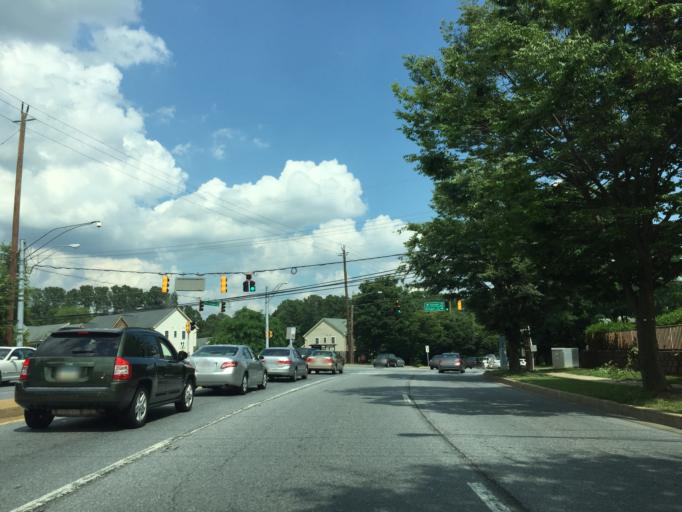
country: US
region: Maryland
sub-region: Montgomery County
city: Colesville
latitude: 39.0755
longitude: -76.9946
